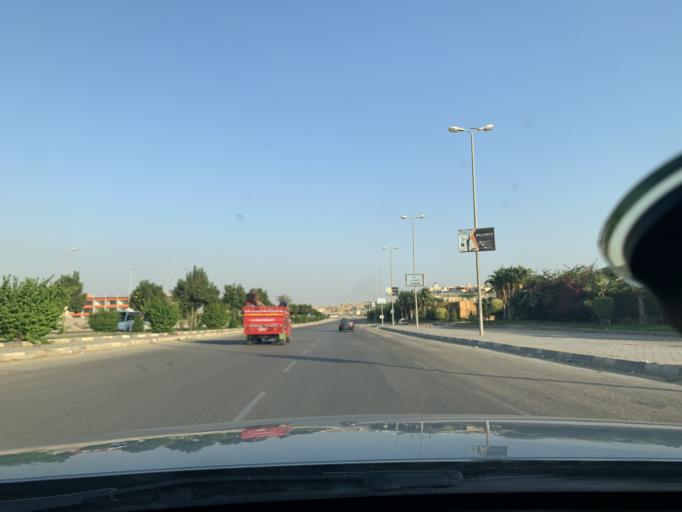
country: EG
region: Muhafazat al Qalyubiyah
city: Al Khankah
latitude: 30.0455
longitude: 31.5202
